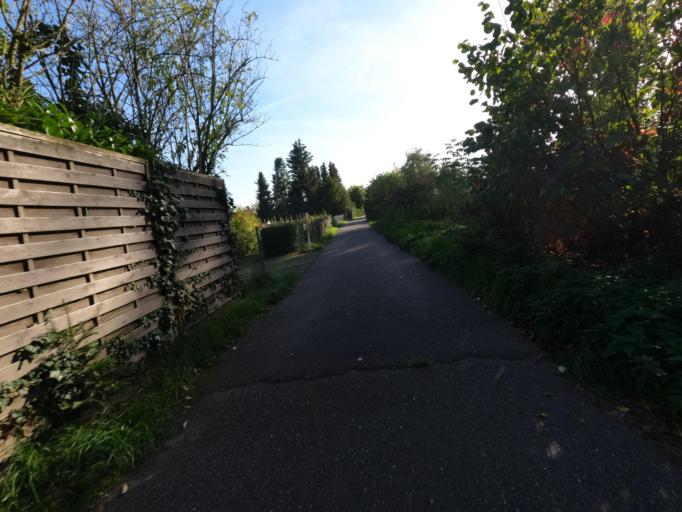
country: DE
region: North Rhine-Westphalia
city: Wegberg
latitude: 51.1641
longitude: 6.2824
